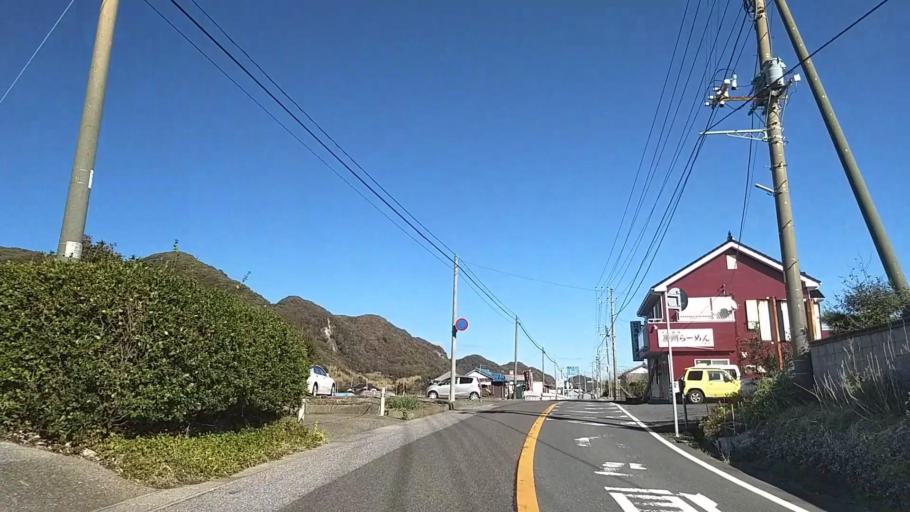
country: JP
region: Chiba
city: Tateyama
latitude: 34.9247
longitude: 139.9399
